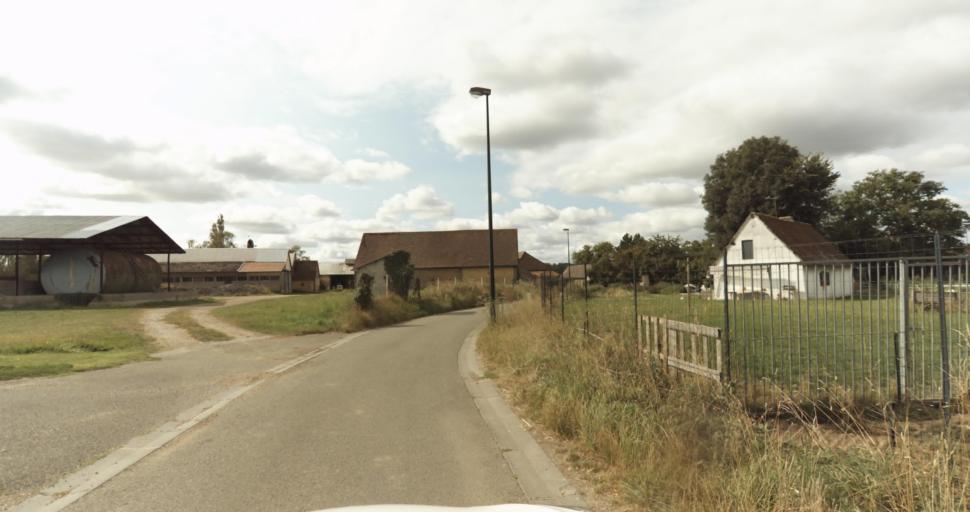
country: FR
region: Haute-Normandie
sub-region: Departement de l'Eure
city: Tillieres-sur-Avre
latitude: 48.7794
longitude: 1.1043
